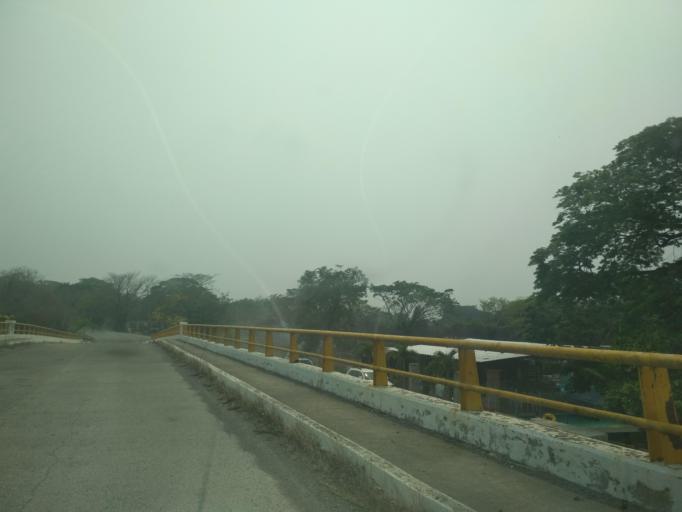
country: MX
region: Veracruz
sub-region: Veracruz
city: Delfino Victoria (Santa Fe)
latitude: 19.1906
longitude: -96.3076
